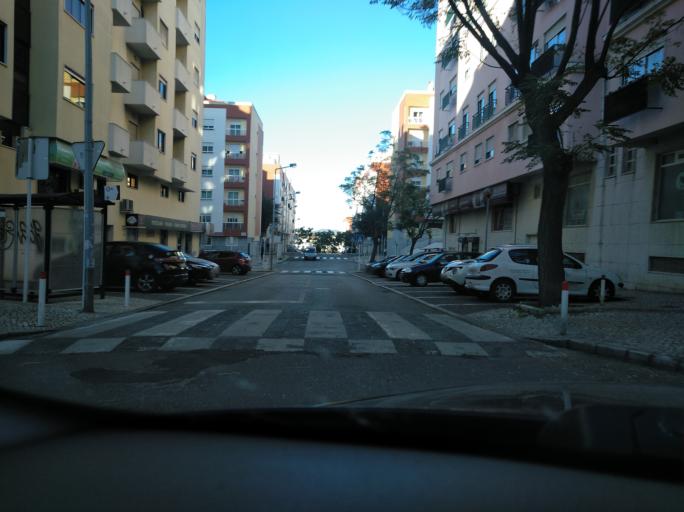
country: PT
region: Lisbon
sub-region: Loures
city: Sacavem
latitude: 38.7925
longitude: -9.1208
